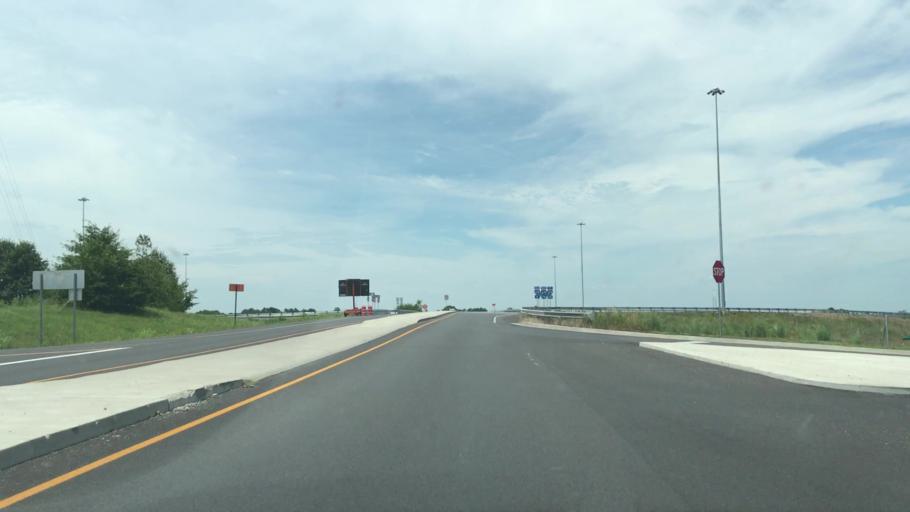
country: US
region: Kentucky
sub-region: Marshall County
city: Benton
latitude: 36.8678
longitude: -88.3621
